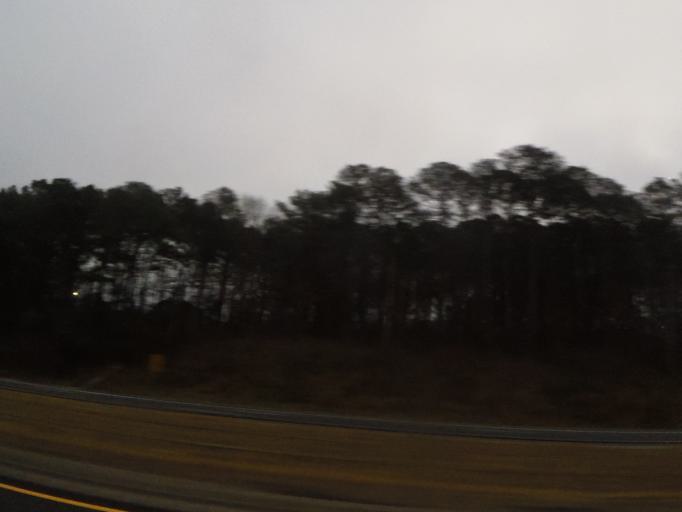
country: US
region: Alabama
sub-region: Cullman County
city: Cullman
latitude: 34.2044
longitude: -86.8784
